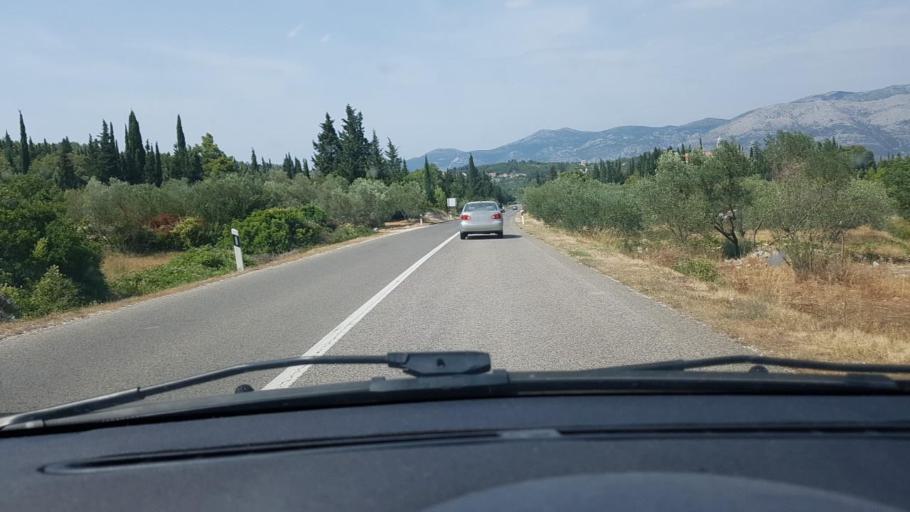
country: HR
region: Dubrovacko-Neretvanska
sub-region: Grad Korcula
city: Zrnovo
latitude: 42.9386
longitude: 17.1045
